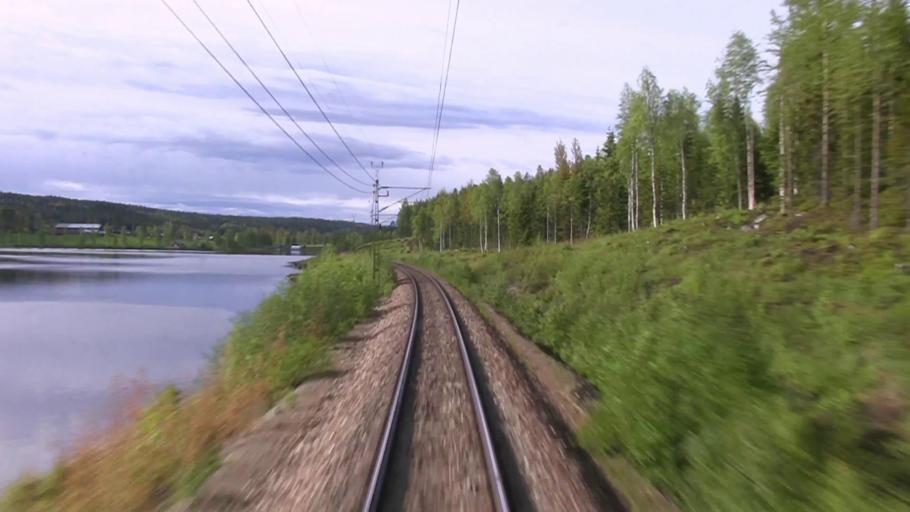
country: SE
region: Vaesterbotten
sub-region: Vindelns Kommun
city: Vindeln
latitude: 64.1146
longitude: 19.6912
